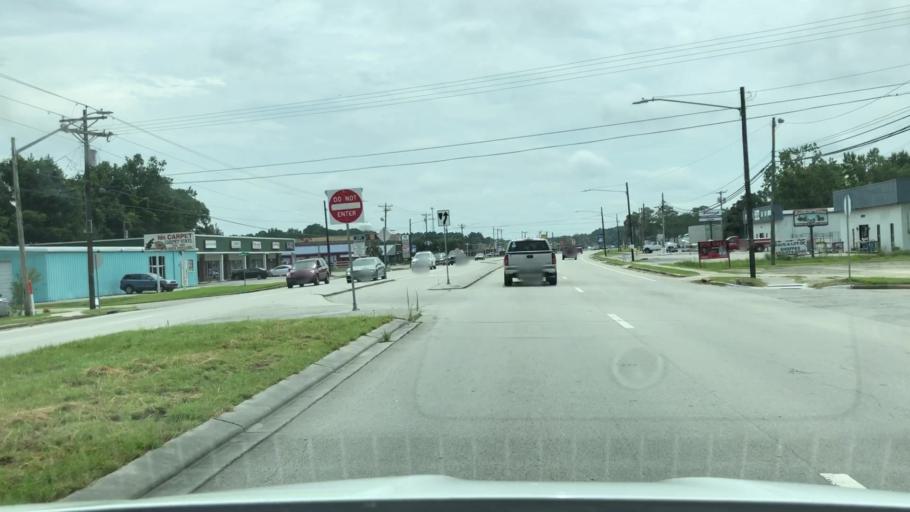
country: US
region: North Carolina
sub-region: Craven County
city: Havelock
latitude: 34.8673
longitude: -76.8998
